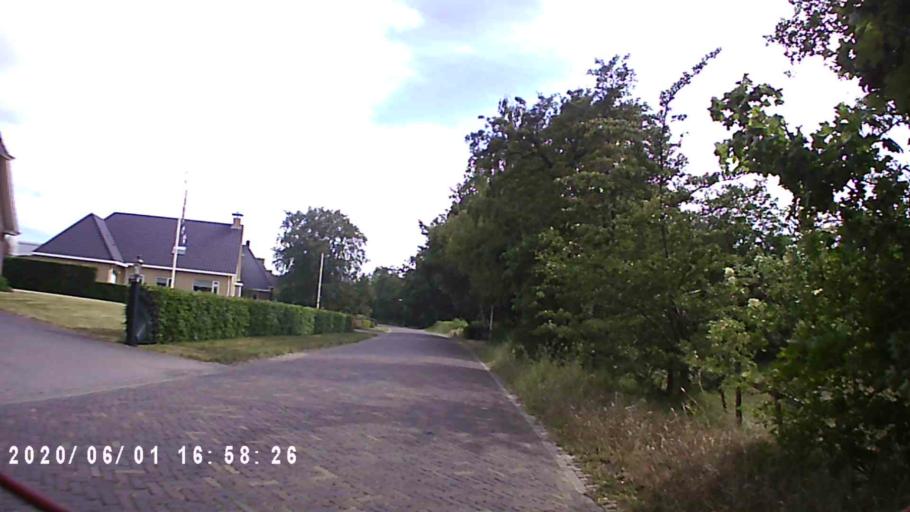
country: NL
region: Friesland
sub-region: Gemeente Tytsjerksteradiel
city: Hurdegaryp
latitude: 53.1894
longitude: 5.9272
